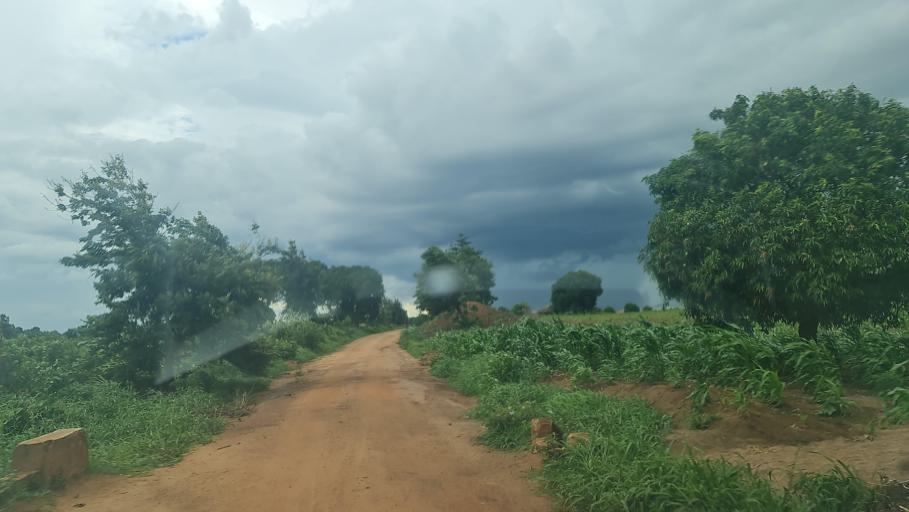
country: MW
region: Southern Region
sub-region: Nsanje District
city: Nsanje
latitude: -17.3840
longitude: 35.5789
